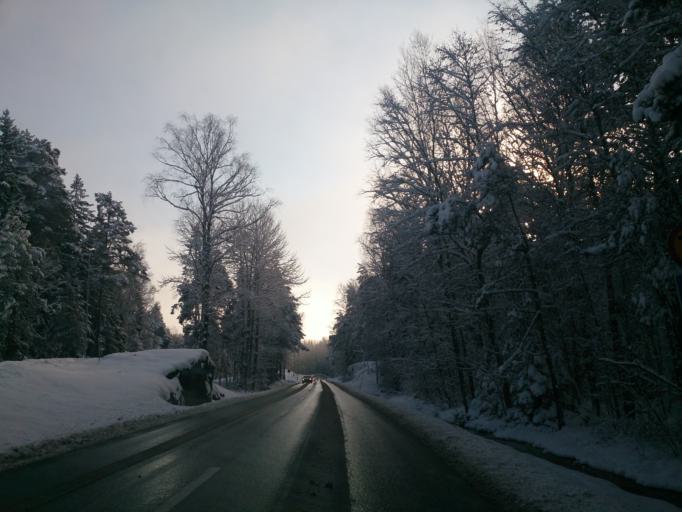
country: SE
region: Stockholm
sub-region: Varmdo Kommun
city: Hemmesta
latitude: 59.2921
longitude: 18.5211
